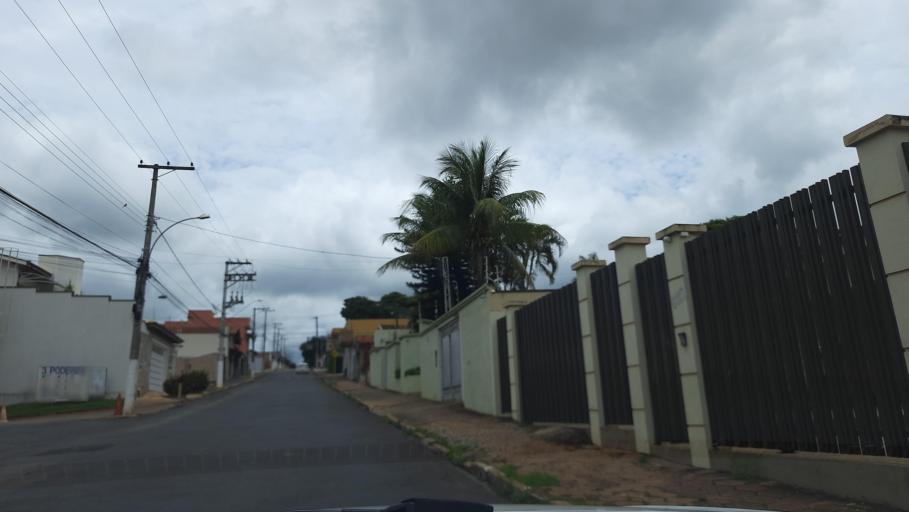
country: BR
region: Sao Paulo
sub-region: Casa Branca
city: Casa Branca
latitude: -21.7783
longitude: -47.0912
